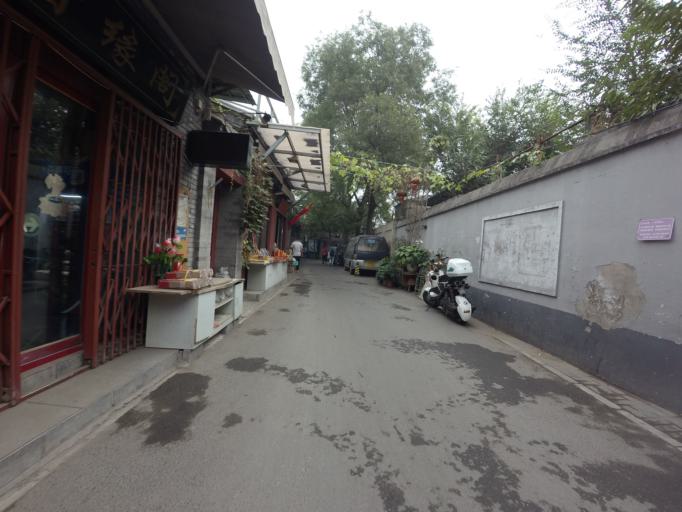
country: CN
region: Beijing
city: Jingshan
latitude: 39.9390
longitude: 116.3851
